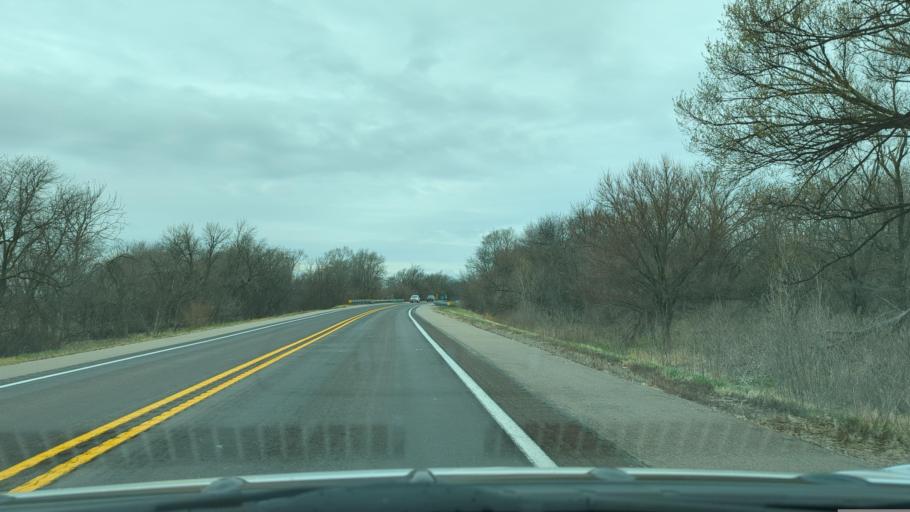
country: US
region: Nebraska
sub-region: Lancaster County
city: Waverly
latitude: 40.9527
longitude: -96.4512
